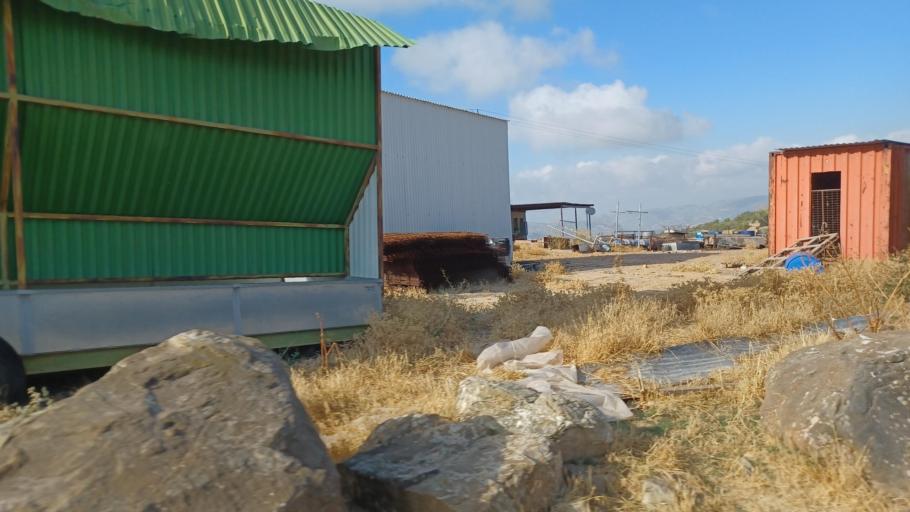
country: CY
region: Pafos
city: Mesogi
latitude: 34.8614
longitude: 32.5962
